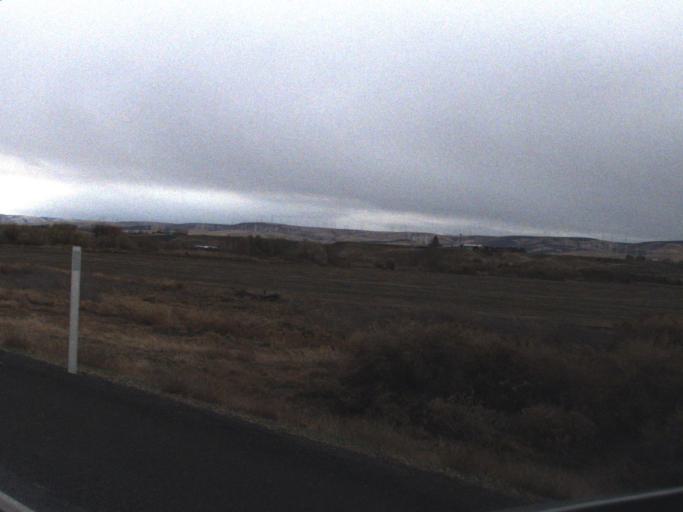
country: US
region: Washington
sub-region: Walla Walla County
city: Garrett
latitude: 46.0417
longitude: -118.6873
